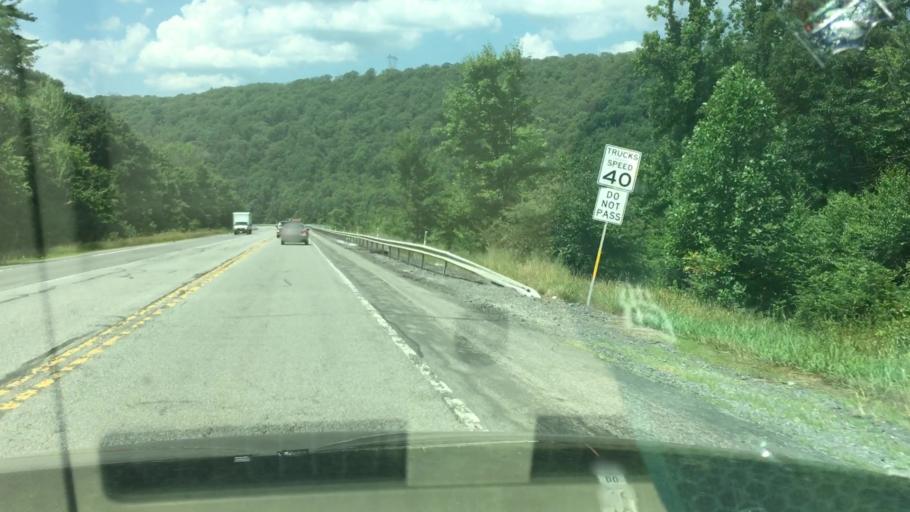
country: US
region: Pennsylvania
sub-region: Schuylkill County
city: Ashland
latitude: 40.7240
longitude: -76.3528
